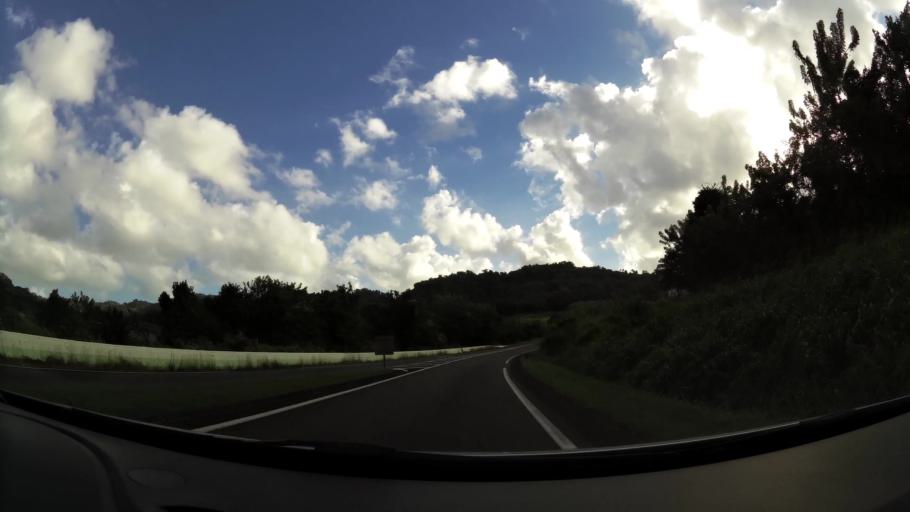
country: MQ
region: Martinique
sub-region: Martinique
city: Ducos
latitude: 14.6031
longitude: -60.9630
